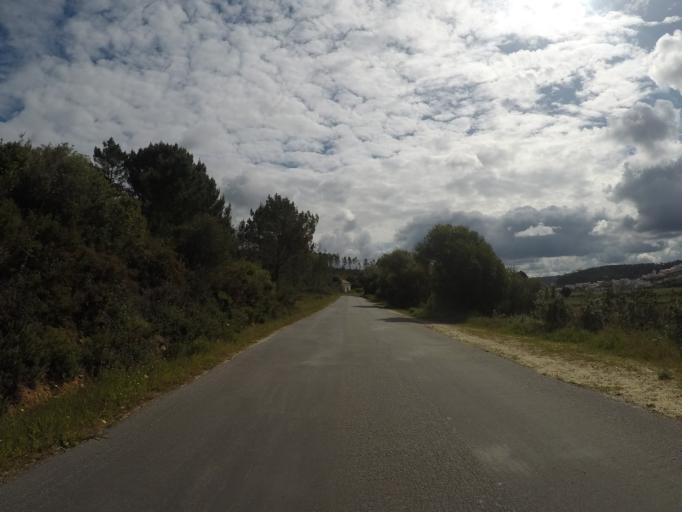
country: PT
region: Beja
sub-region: Odemira
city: Sao Teotonio
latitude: 37.4354
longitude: -8.7817
